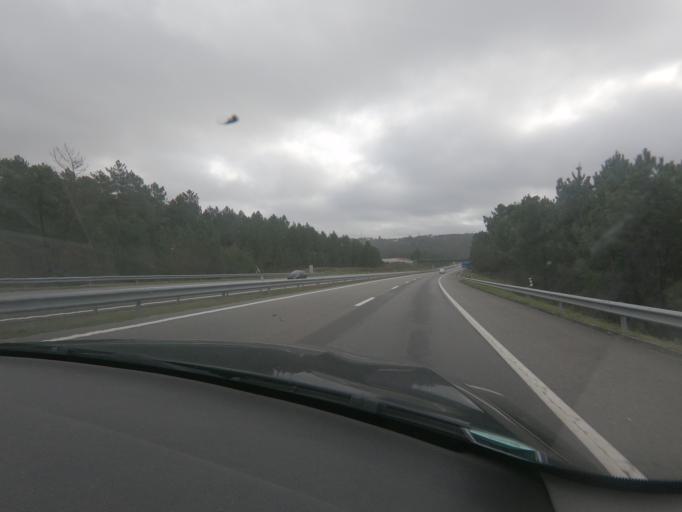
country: PT
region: Viseu
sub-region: Castro Daire
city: Castro Daire
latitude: 40.8529
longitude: -7.9281
